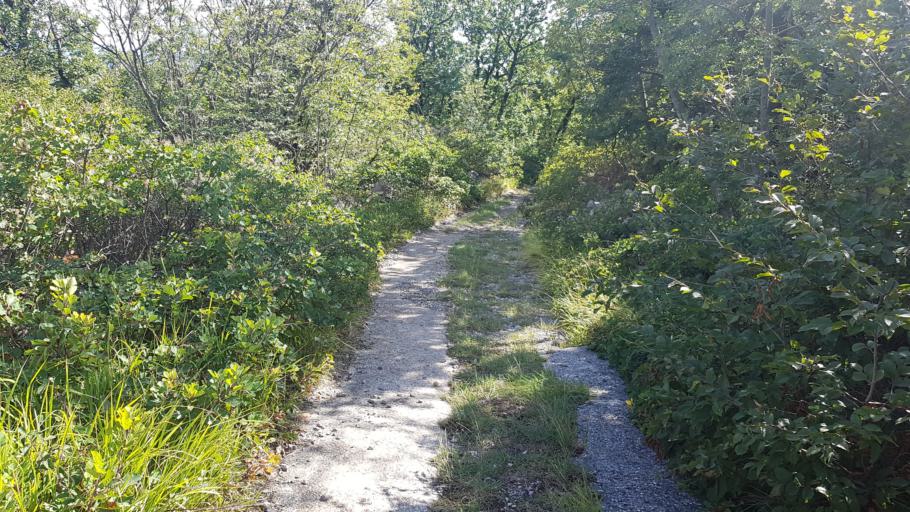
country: IT
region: Friuli Venezia Giulia
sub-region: Provincia di Trieste
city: Sistiana-Visogliano
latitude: 45.7927
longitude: 13.6262
